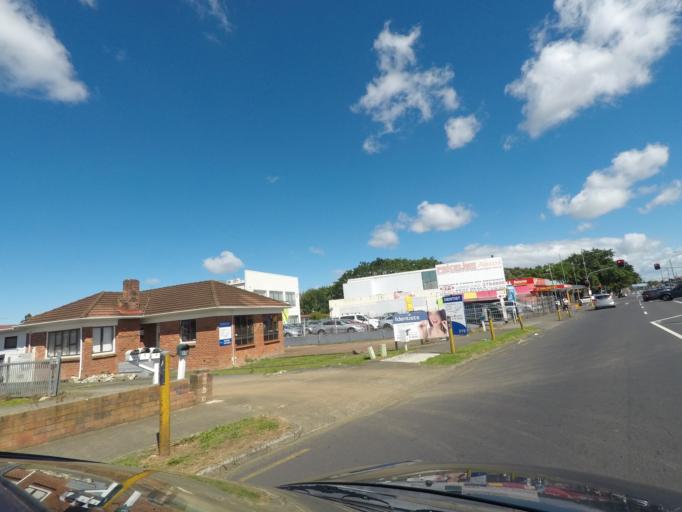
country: NZ
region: Auckland
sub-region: Auckland
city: Manukau City
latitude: -36.9745
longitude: 174.8651
